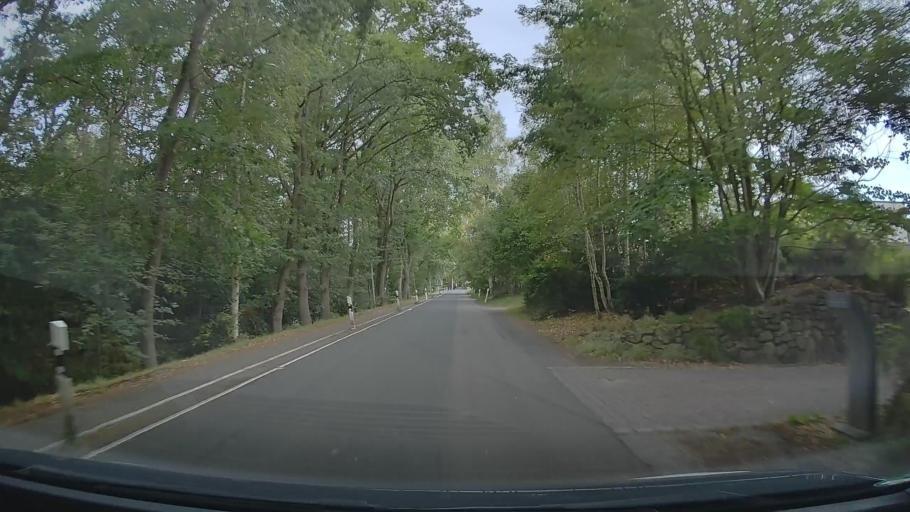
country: DE
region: Lower Saxony
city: Wardenburg
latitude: 53.1100
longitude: 8.1119
